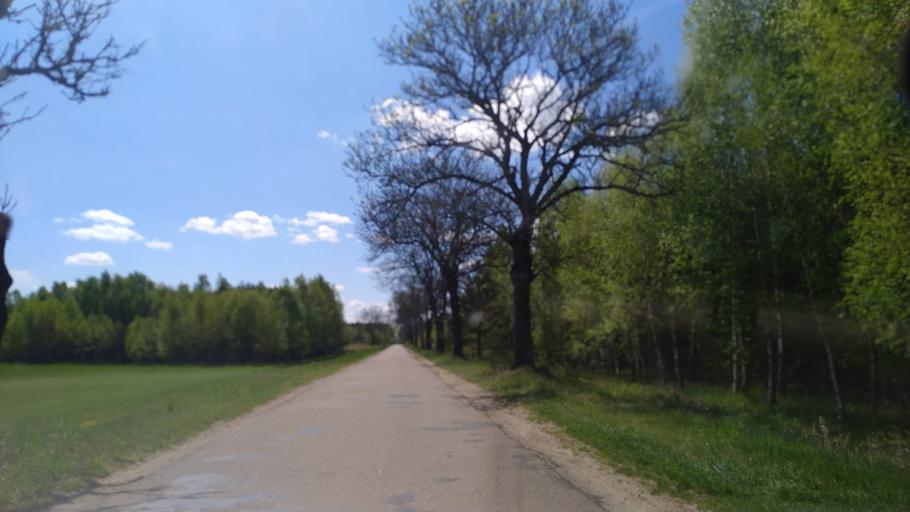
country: PL
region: Greater Poland Voivodeship
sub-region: Powiat zlotowski
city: Tarnowka
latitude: 53.2695
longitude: 16.7988
